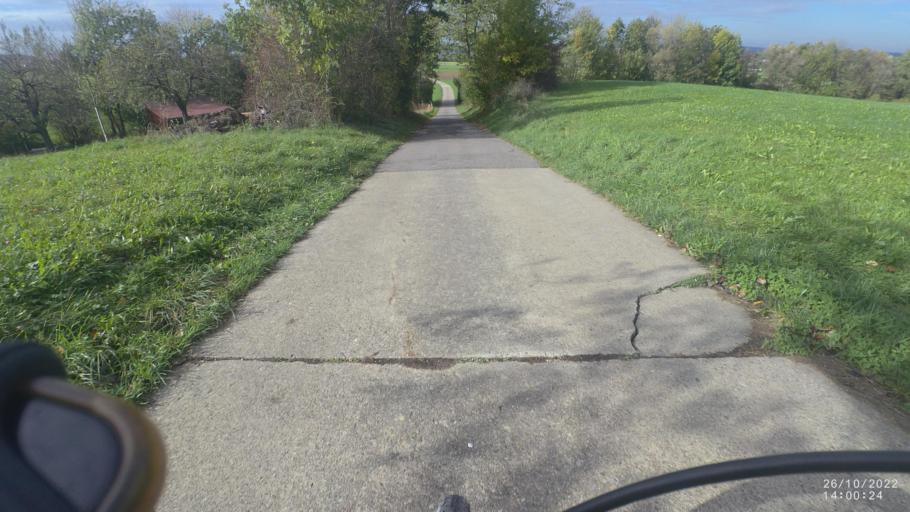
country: DE
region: Baden-Wuerttemberg
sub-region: Regierungsbezirk Stuttgart
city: Gammelshausen
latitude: 48.6430
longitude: 9.6595
